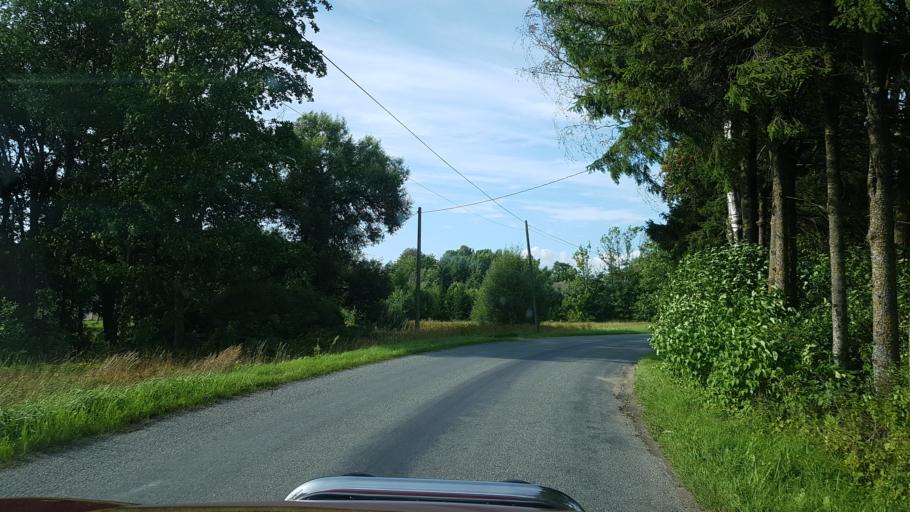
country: EE
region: Laeaene
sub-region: Lihula vald
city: Lihula
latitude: 58.4434
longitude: 24.0029
